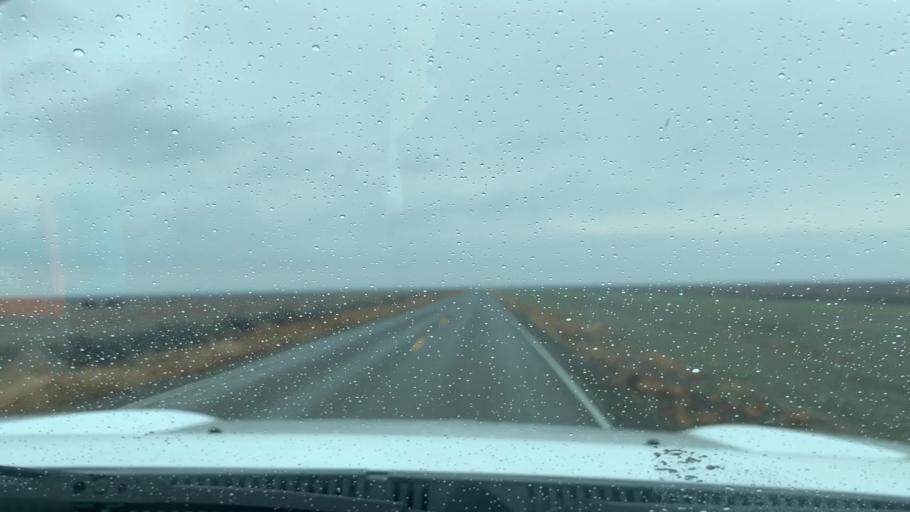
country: US
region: California
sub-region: Kings County
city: Corcoran
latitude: 35.9339
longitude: -119.7094
